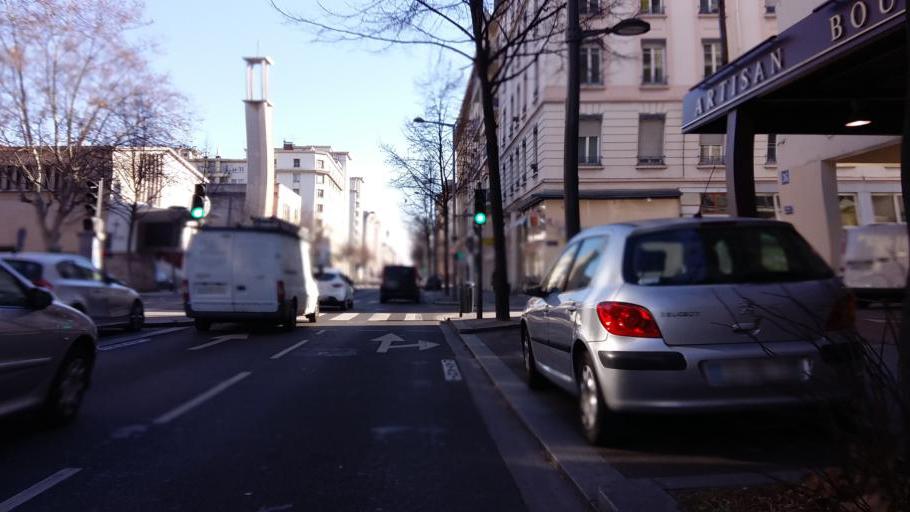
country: FR
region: Rhone-Alpes
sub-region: Departement du Rhone
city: Lyon
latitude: 45.7464
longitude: 4.8380
